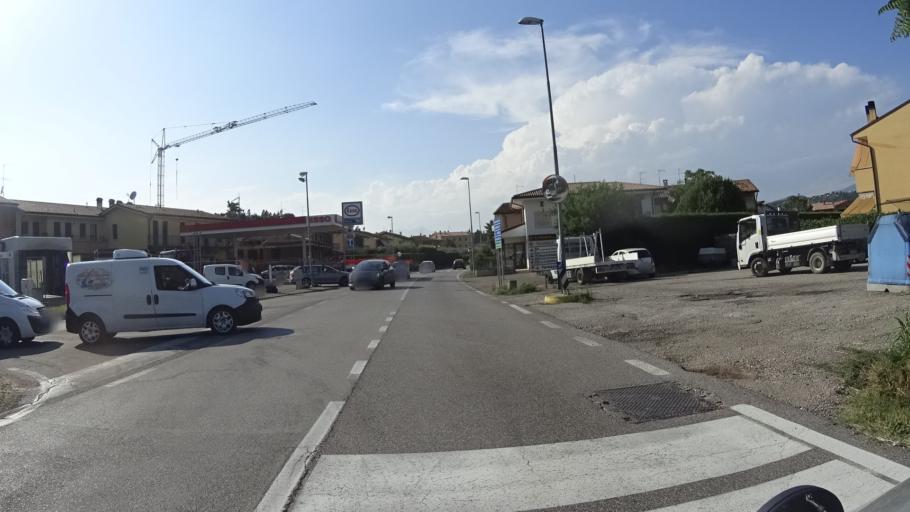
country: IT
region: Veneto
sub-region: Provincia di Verona
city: Calmasino
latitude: 45.5197
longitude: 10.7580
